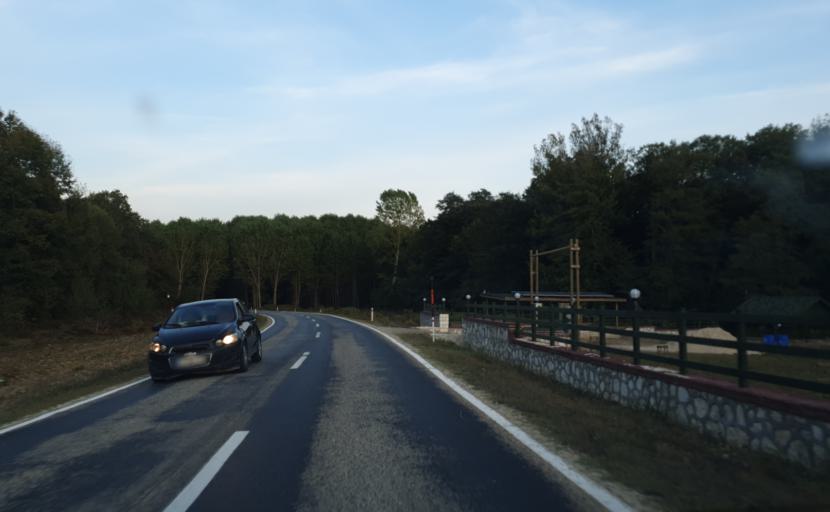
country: TR
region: Kirklareli
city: Igneada
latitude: 41.8757
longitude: 27.9126
